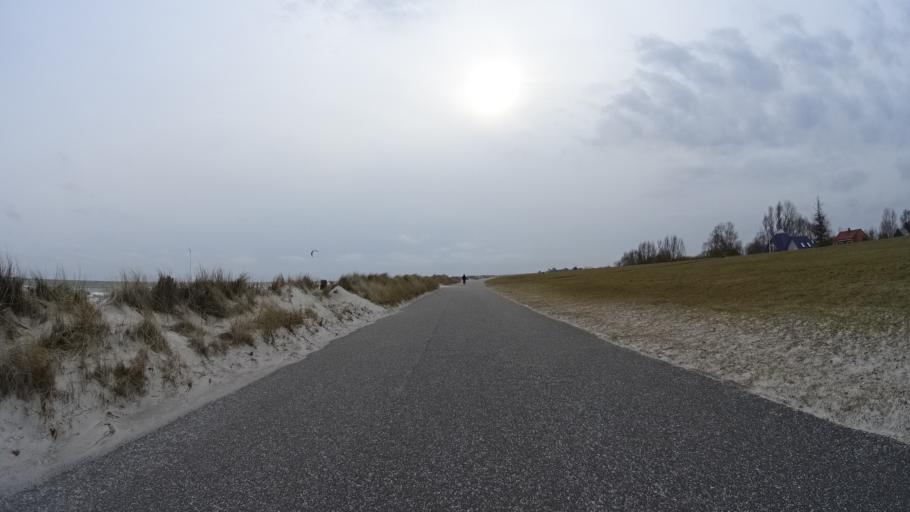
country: DE
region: Schleswig-Holstein
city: Wisch
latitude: 54.4257
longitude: 10.3887
